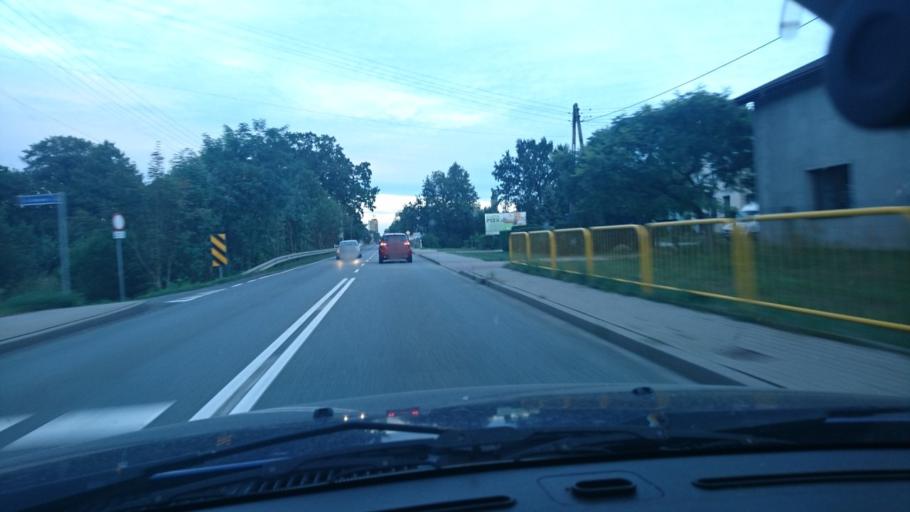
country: PL
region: Silesian Voivodeship
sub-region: Powiat tarnogorski
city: Zbroslawice
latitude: 50.4823
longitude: 18.7889
